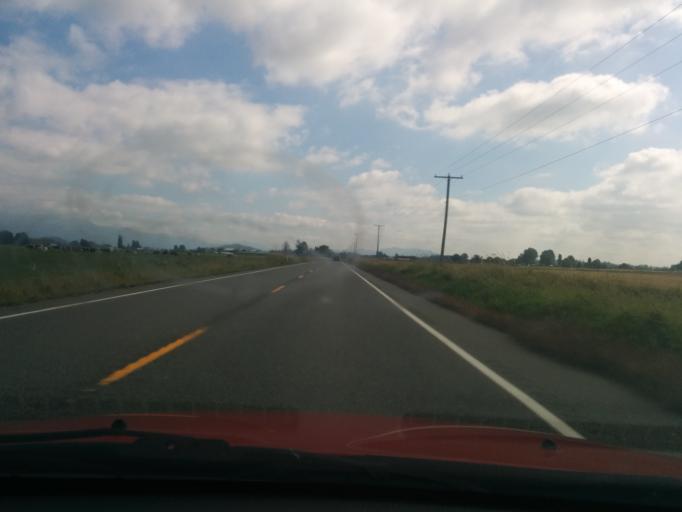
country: US
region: Washington
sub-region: Skagit County
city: Burlington
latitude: 48.5400
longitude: -122.4007
